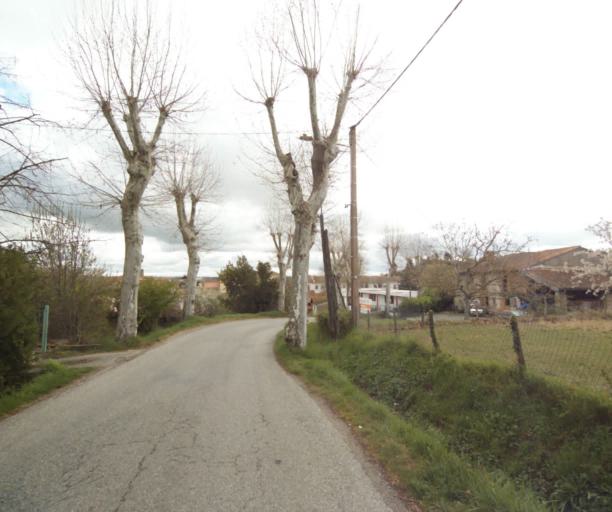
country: FR
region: Midi-Pyrenees
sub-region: Departement de l'Ariege
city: Saverdun
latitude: 43.2331
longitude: 1.5721
